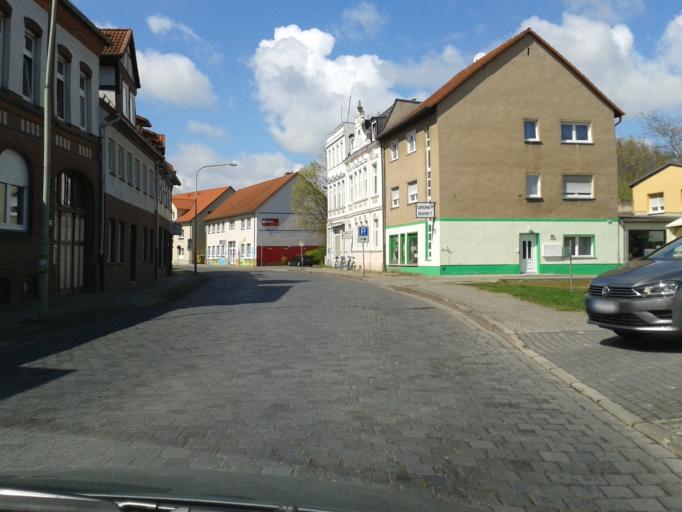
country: DE
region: Saxony-Anhalt
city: Salzwedel
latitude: 52.8483
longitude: 11.1572
